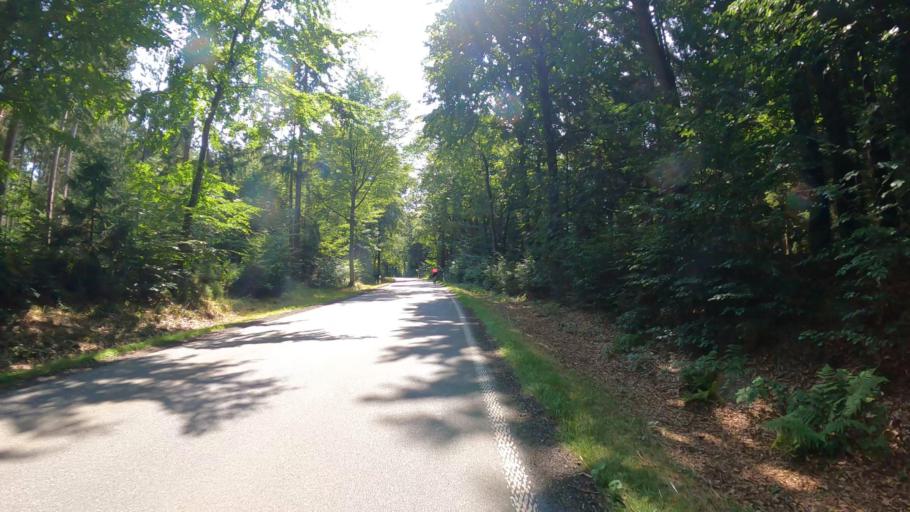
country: DE
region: Schleswig-Holstein
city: Heidmuhlen
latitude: 53.9589
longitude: 10.1313
